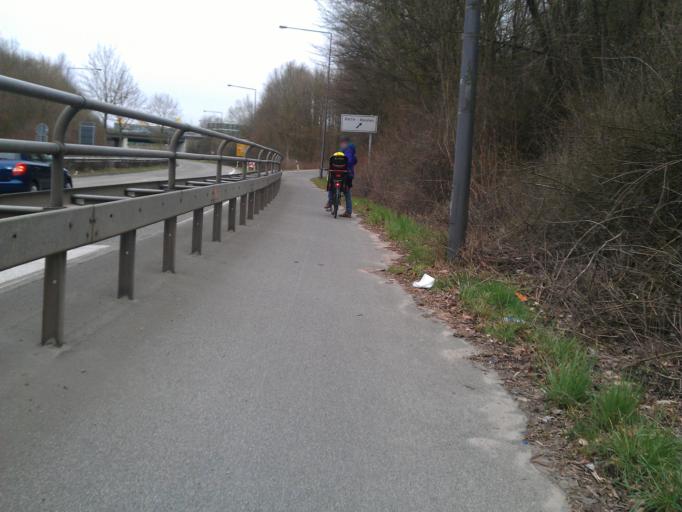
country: DE
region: North Rhine-Westphalia
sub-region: Regierungsbezirk Koln
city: Aachen
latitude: 50.7895
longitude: 6.0528
